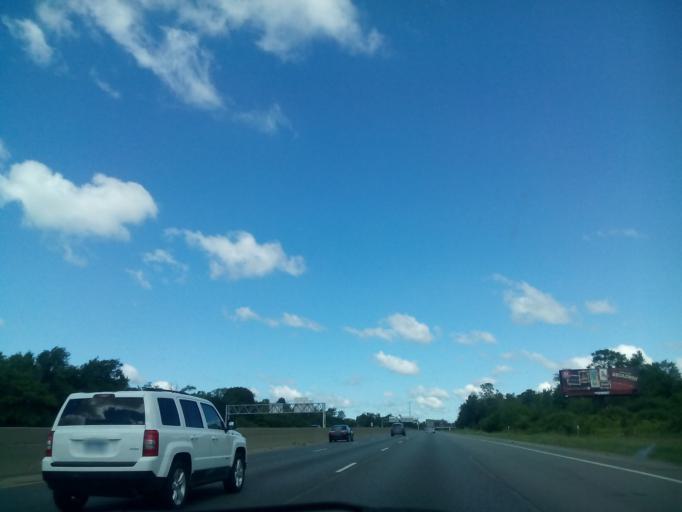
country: US
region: Michigan
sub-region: Genesee County
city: Flint
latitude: 42.9921
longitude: -83.7424
